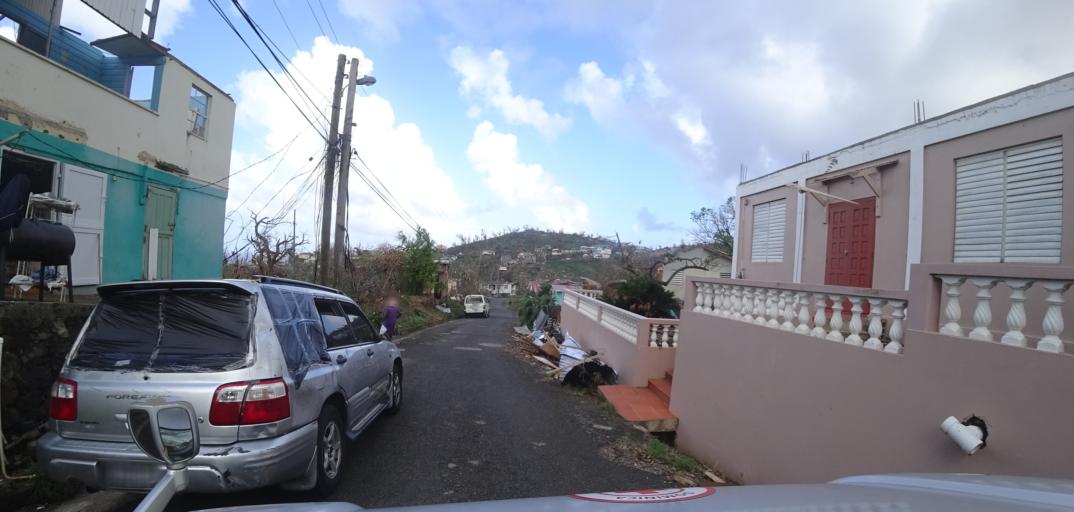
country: DM
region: Saint Andrew
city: Marigot
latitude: 15.5386
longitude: -61.2877
